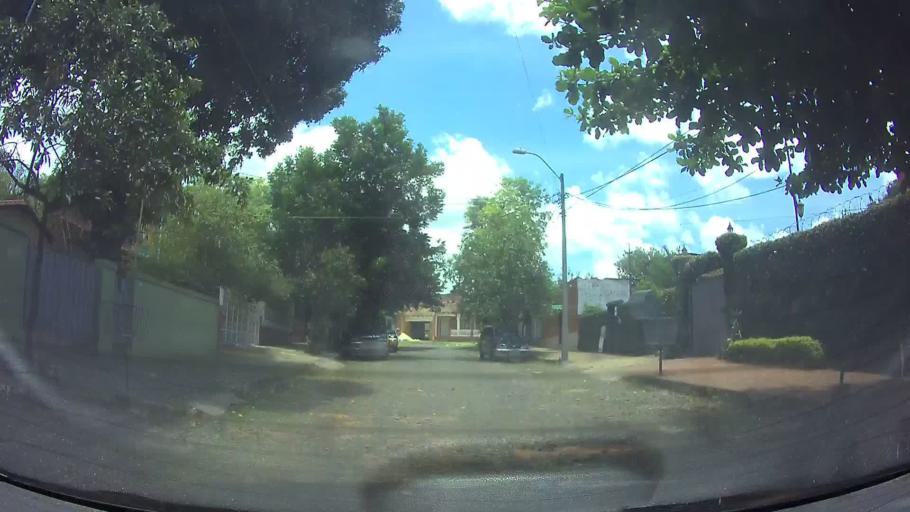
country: PY
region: Asuncion
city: Asuncion
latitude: -25.2731
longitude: -57.5911
